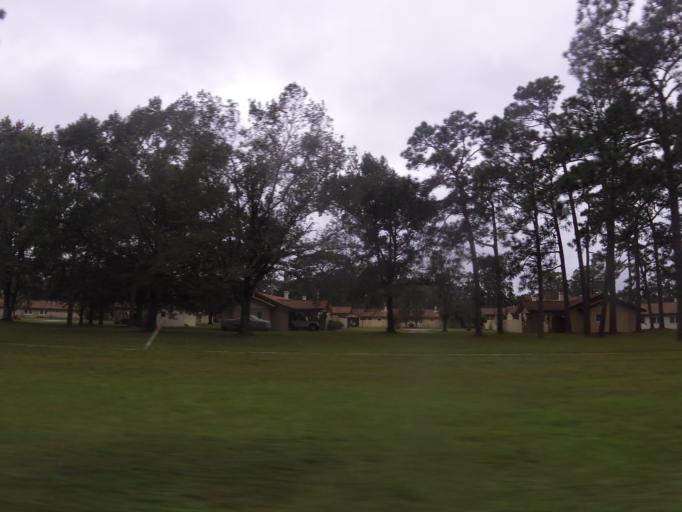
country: US
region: Florida
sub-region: Duval County
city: Baldwin
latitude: 30.2354
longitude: -81.8898
